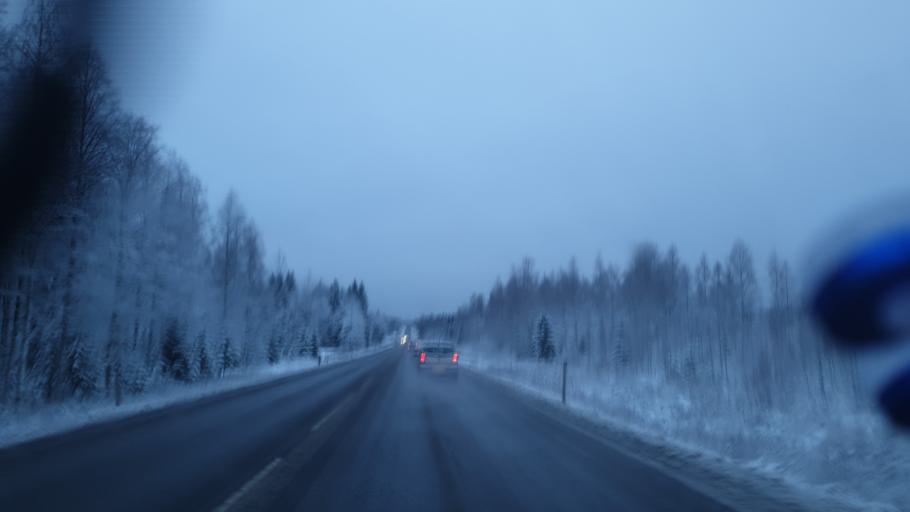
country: FI
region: Central Finland
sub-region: Saarijaervi-Viitasaari
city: Viitasaari
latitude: 63.0279
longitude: 25.8138
